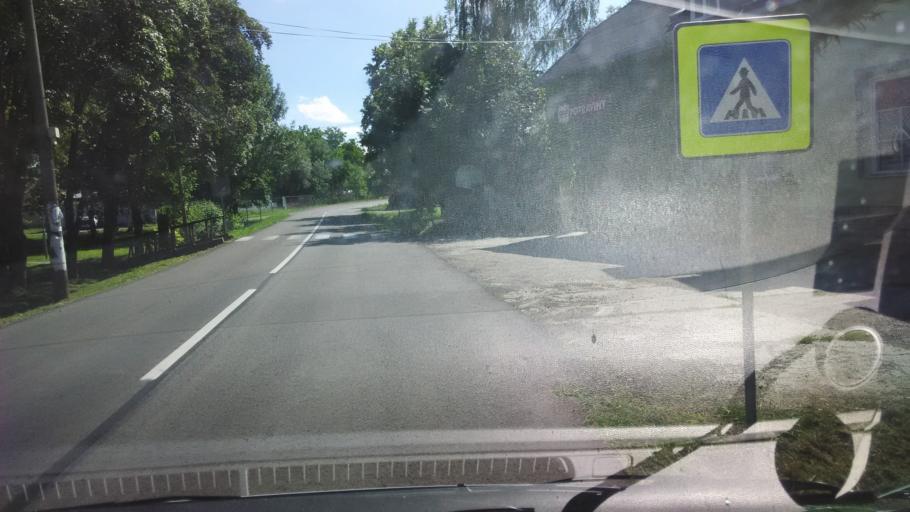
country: SK
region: Nitriansky
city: Tlmace
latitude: 48.1568
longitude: 18.4499
